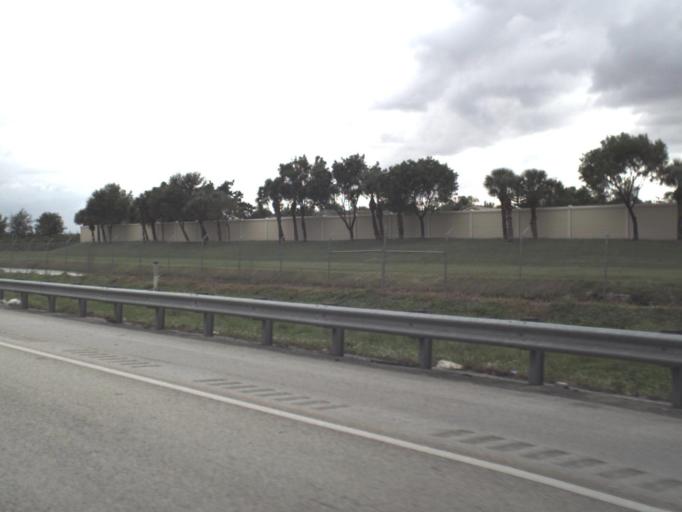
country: US
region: Florida
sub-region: Palm Beach County
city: Seminole Manor
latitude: 26.5519
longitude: -80.1730
